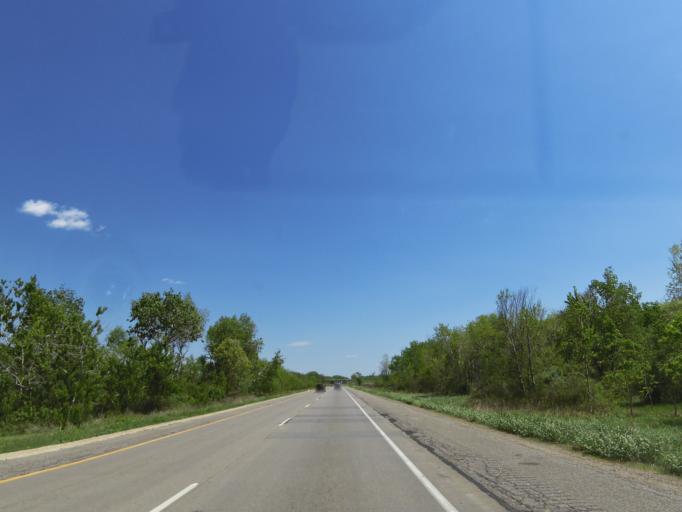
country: US
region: Wisconsin
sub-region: Juneau County
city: Mauston
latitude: 43.7776
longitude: -90.0237
